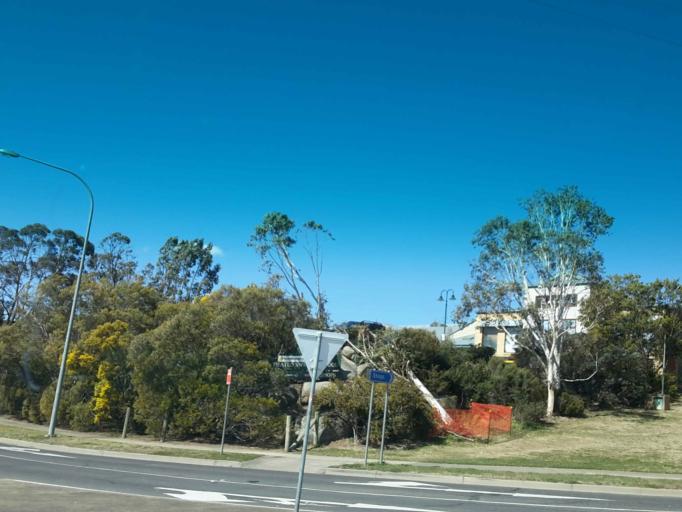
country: AU
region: New South Wales
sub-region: Snowy River
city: Jindabyne
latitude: -36.4149
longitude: 148.6188
